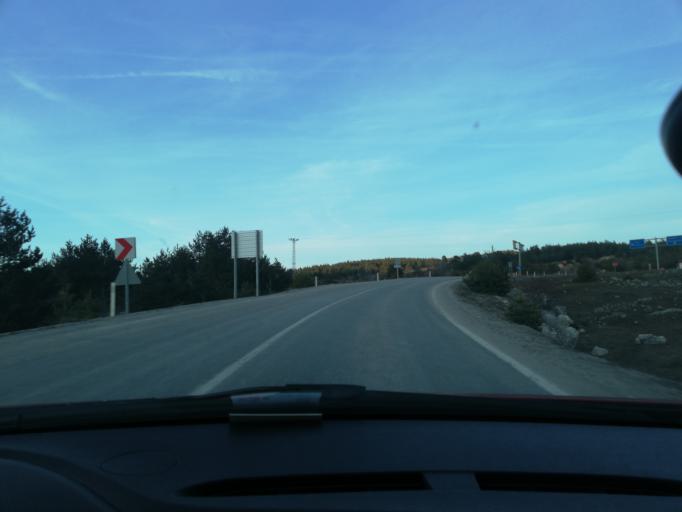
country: TR
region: Kastamonu
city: Agli
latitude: 41.7154
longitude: 33.6539
